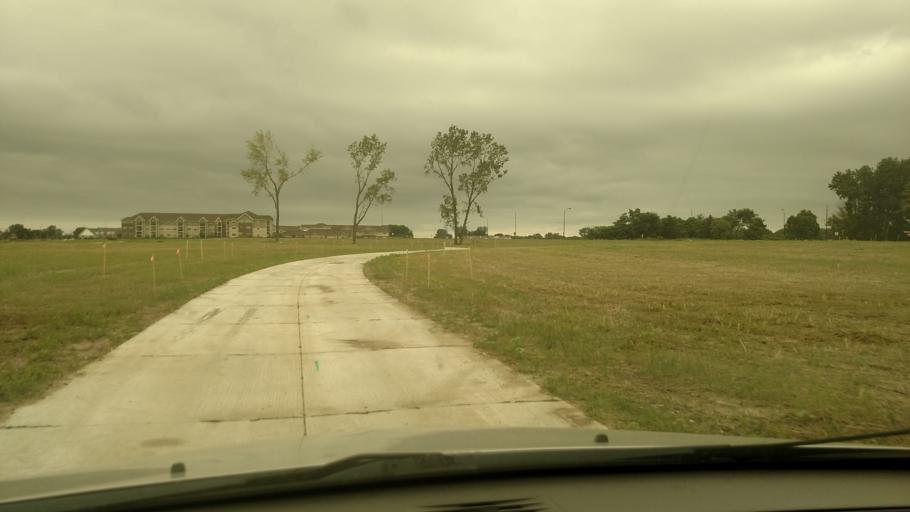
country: US
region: Iowa
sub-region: Polk County
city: Ankeny
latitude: 41.7145
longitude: -93.6133
